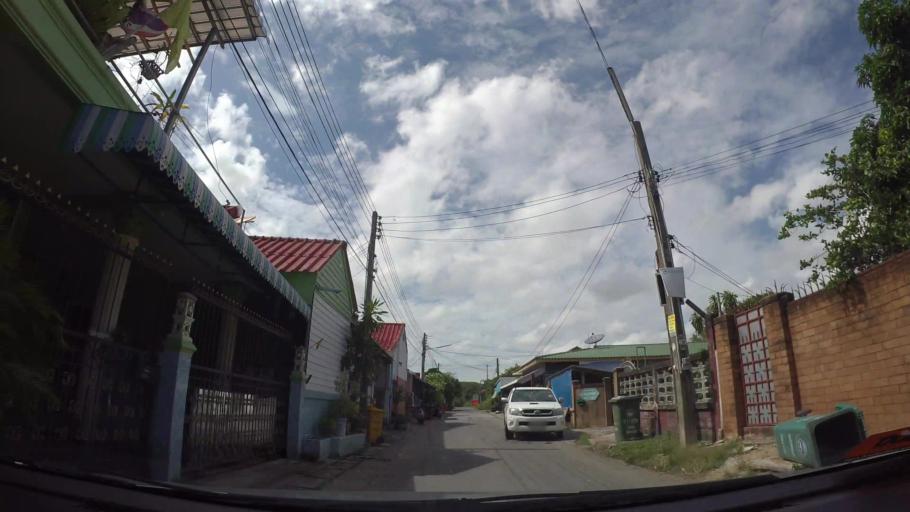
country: TH
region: Chon Buri
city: Sattahip
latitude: 12.6891
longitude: 100.8983
